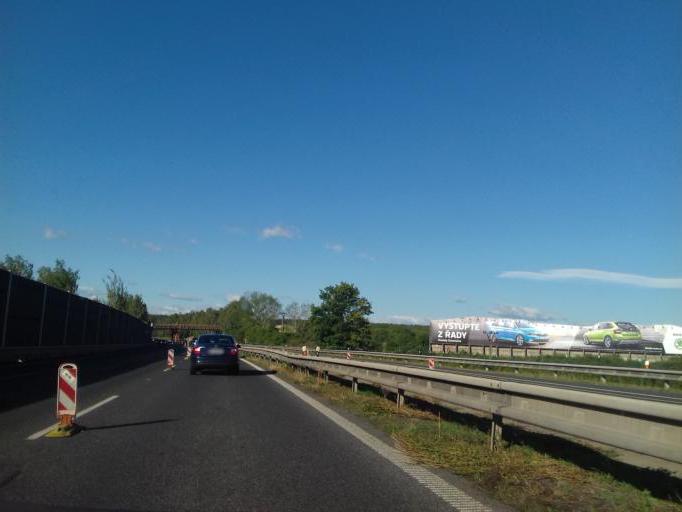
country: CZ
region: Central Bohemia
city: Lustenice
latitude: 50.3290
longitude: 14.8760
